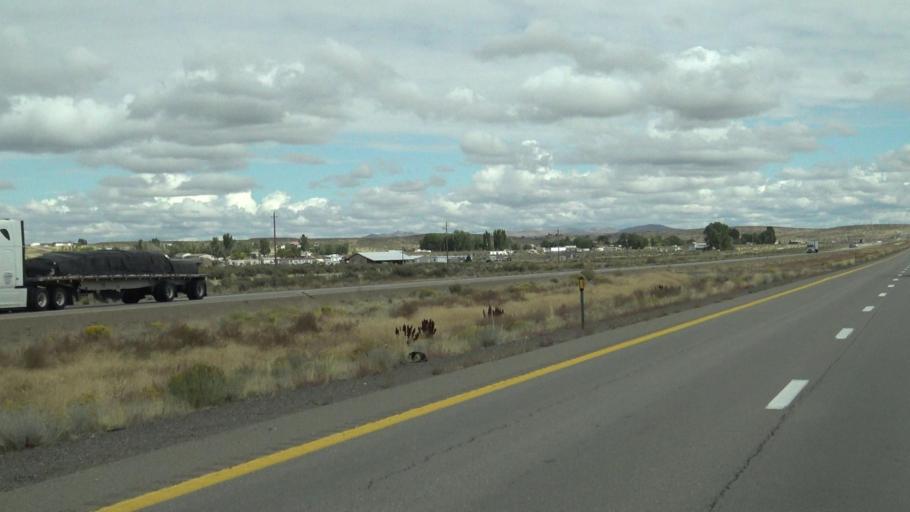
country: US
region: Nevada
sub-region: Elko County
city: Elko
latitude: 40.9365
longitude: -115.6596
